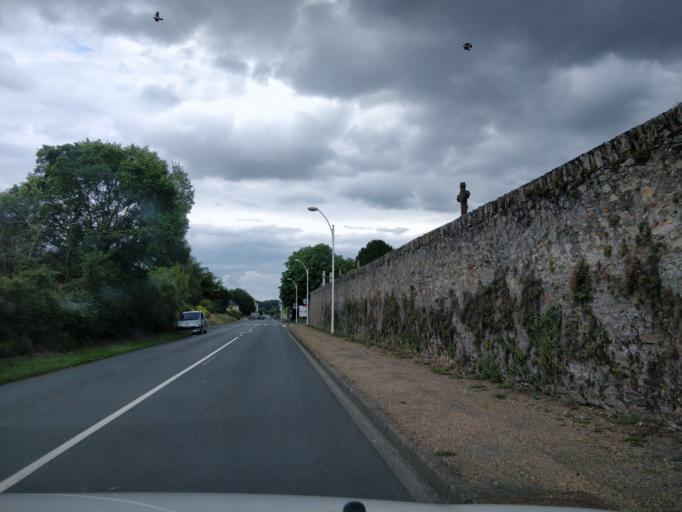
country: FR
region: Pays de la Loire
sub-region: Departement de Maine-et-Loire
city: Grez-Neuville
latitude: 47.6310
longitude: -0.7174
